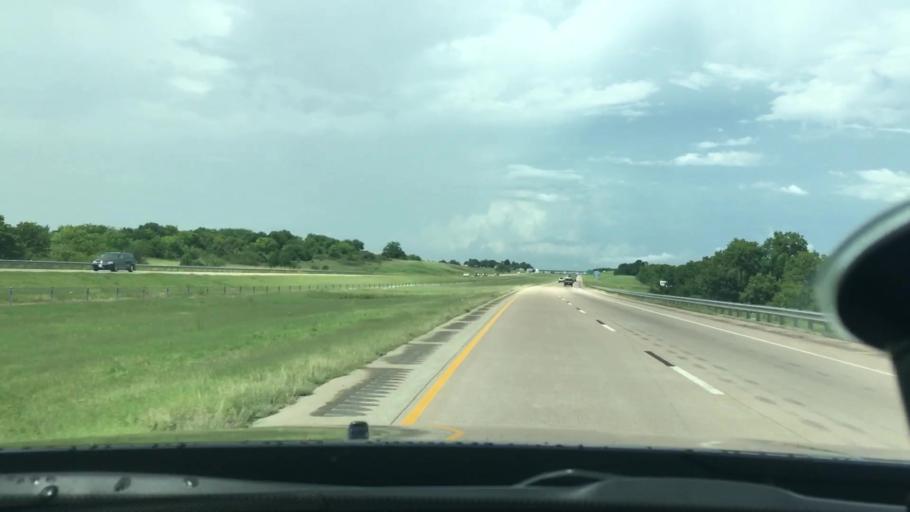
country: US
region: Oklahoma
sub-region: Garvin County
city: Pauls Valley
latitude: 34.7133
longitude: -97.2493
